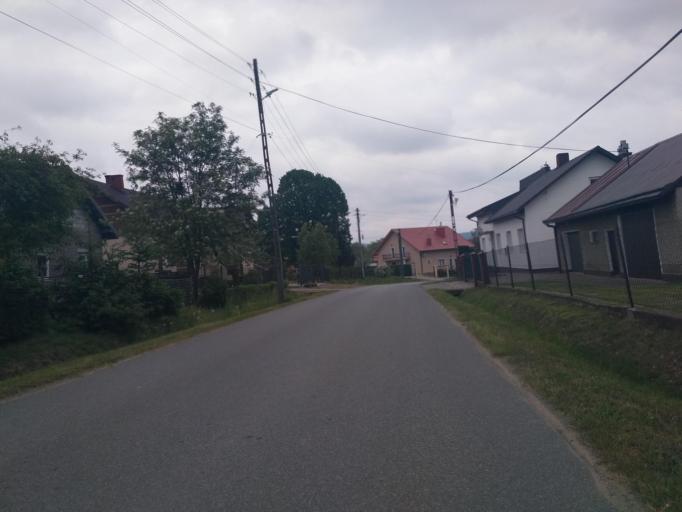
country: PL
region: Subcarpathian Voivodeship
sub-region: Powiat krosnienski
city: Chorkowka
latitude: 49.6660
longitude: 21.7190
